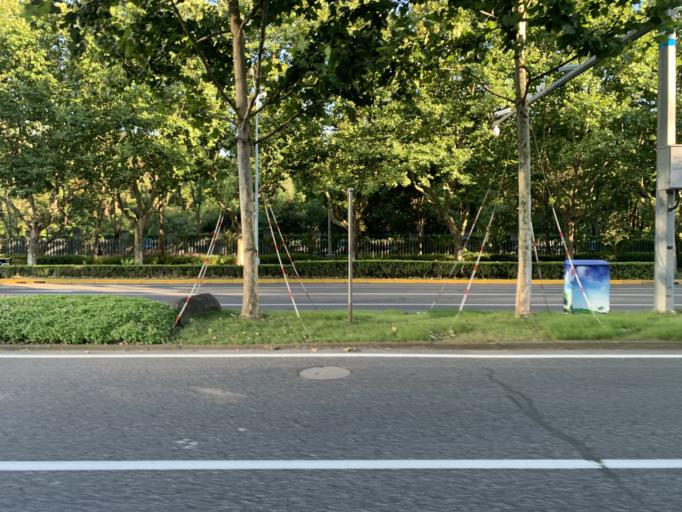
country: CN
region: Shanghai Shi
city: Huamu
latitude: 31.2209
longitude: 121.5439
